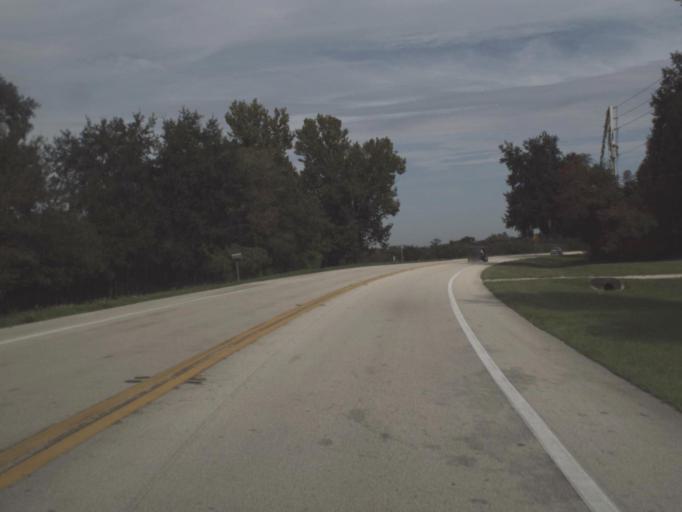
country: US
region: Florida
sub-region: DeSoto County
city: Southeast Arcadia
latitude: 27.1716
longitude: -81.8269
